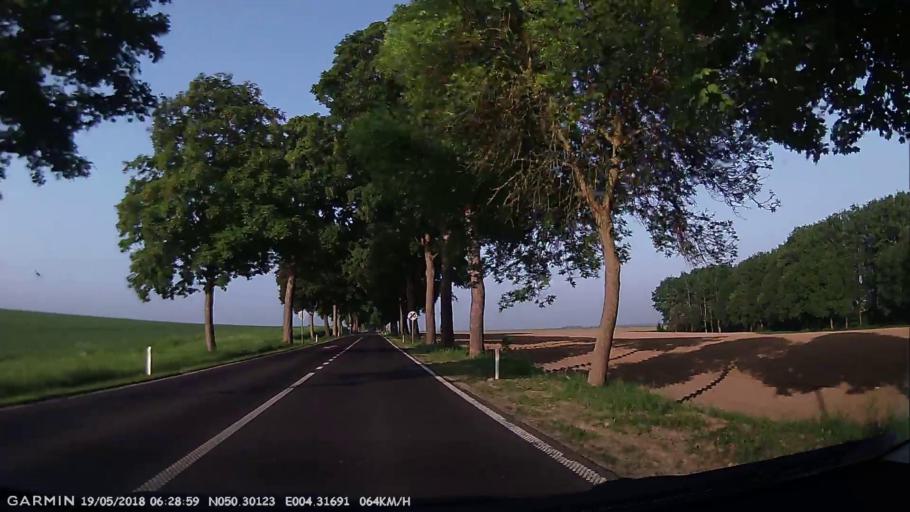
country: BE
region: Wallonia
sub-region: Province du Hainaut
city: Thuin
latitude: 50.3012
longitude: 4.3169
